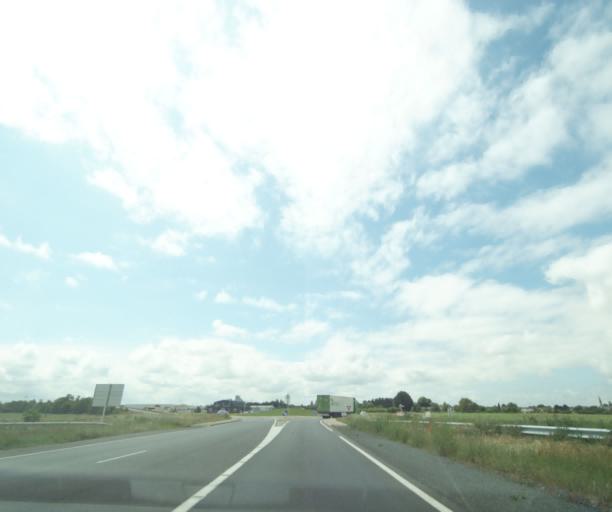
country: FR
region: Poitou-Charentes
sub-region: Departement des Deux-Sevres
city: Sainte-Verge
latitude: 47.0149
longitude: -0.2008
